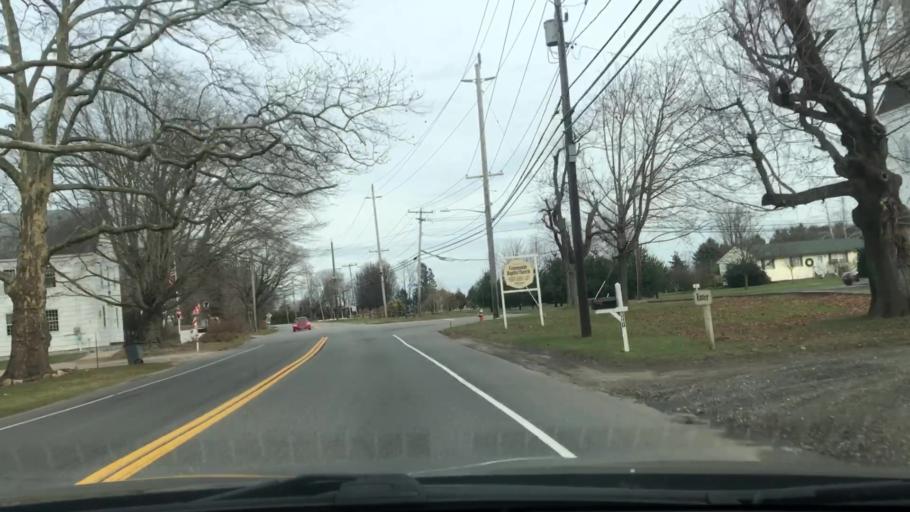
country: US
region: New York
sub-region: Suffolk County
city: Northville
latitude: 40.9697
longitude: -72.6195
